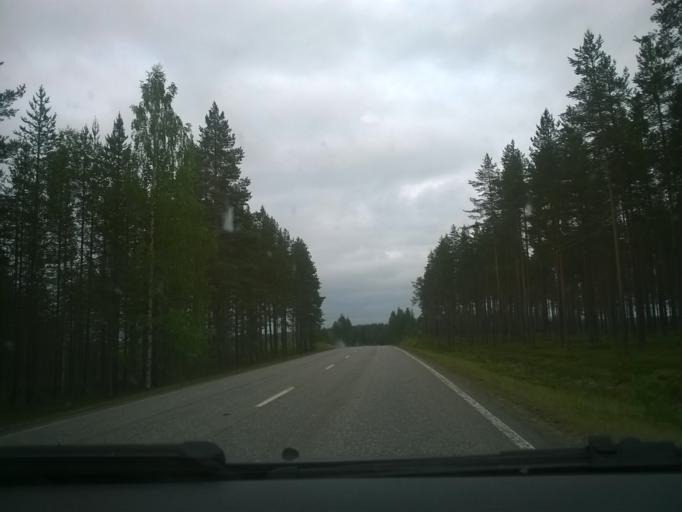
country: FI
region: Kainuu
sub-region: Kehys-Kainuu
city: Kuhmo
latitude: 64.1478
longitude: 29.4174
